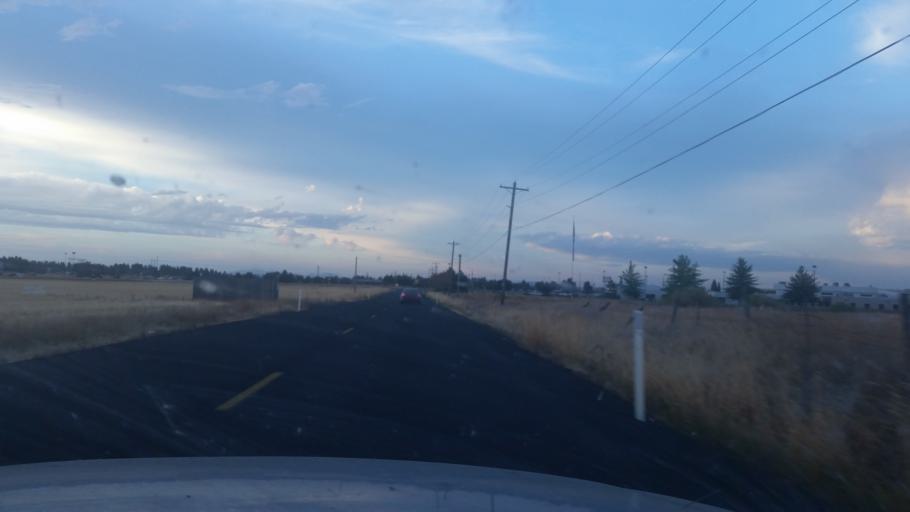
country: US
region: Washington
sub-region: Spokane County
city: Airway Heights
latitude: 47.5840
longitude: -117.5645
